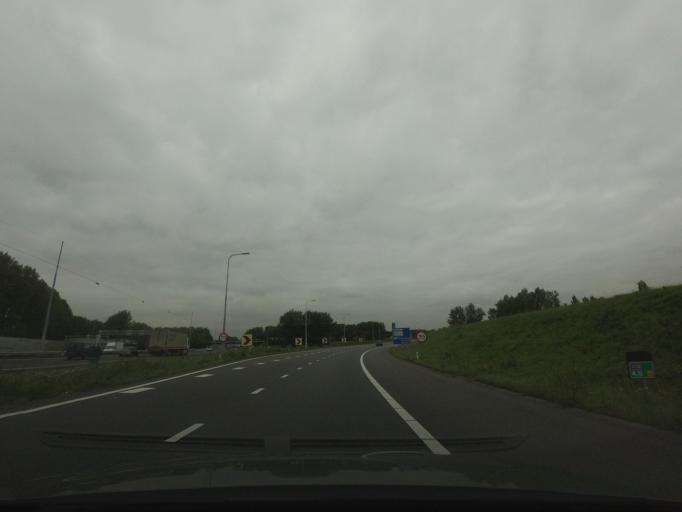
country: NL
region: North Holland
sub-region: Gemeente Landsmeer
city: Landsmeer
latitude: 52.4060
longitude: 4.9449
